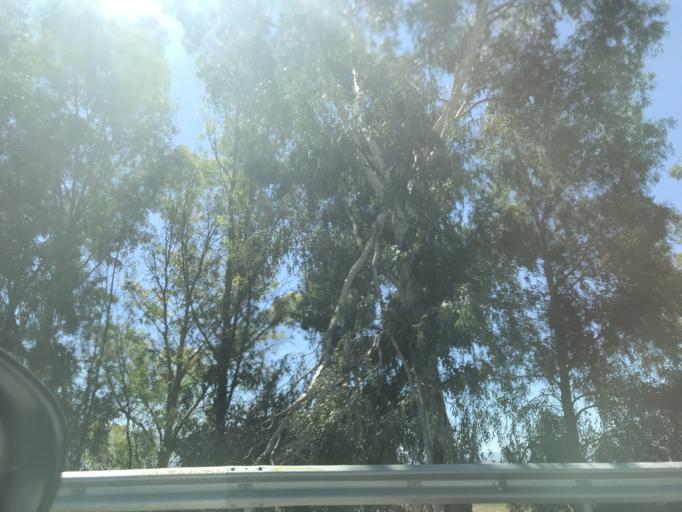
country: TR
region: Aydin
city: Aydin
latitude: 37.8174
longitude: 27.8458
